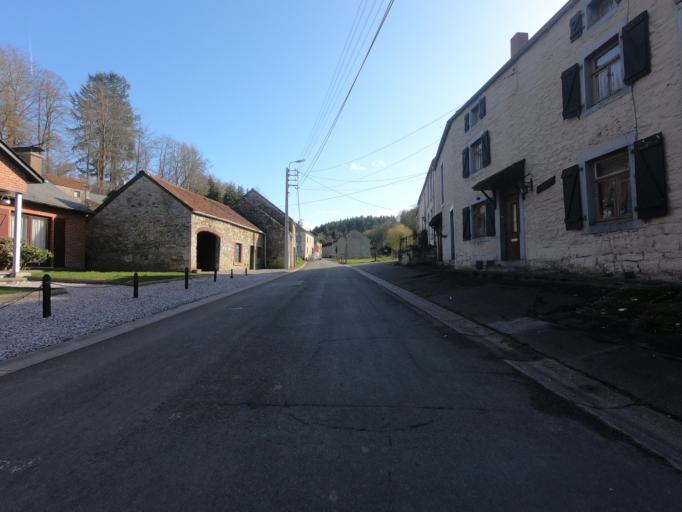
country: BE
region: Wallonia
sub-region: Province de Namur
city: Mettet
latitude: 50.2991
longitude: 4.7525
